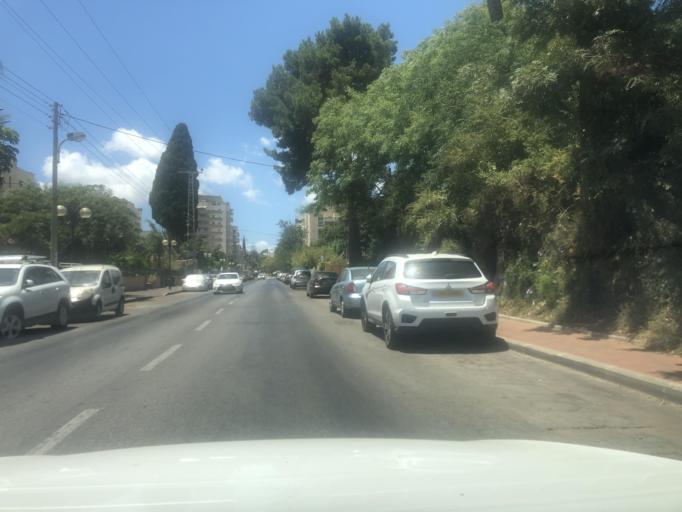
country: IL
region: Central District
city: Hod HaSharon
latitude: 32.1589
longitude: 34.9080
